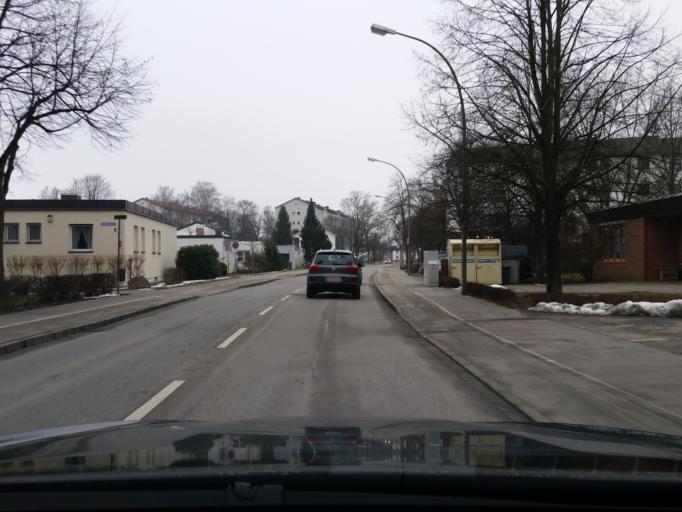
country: DE
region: Bavaria
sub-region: Lower Bavaria
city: Landshut
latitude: 48.5341
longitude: 12.1376
